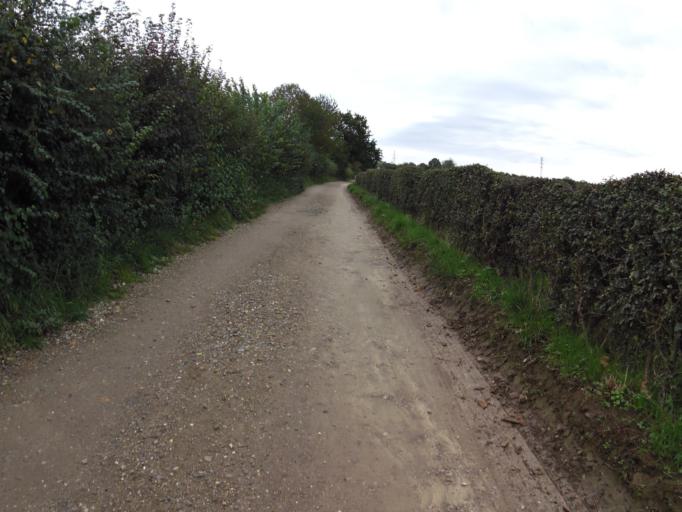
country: NL
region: Limburg
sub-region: Gemeente Voerendaal
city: Ubachsberg
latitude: 50.8644
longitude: 5.9489
